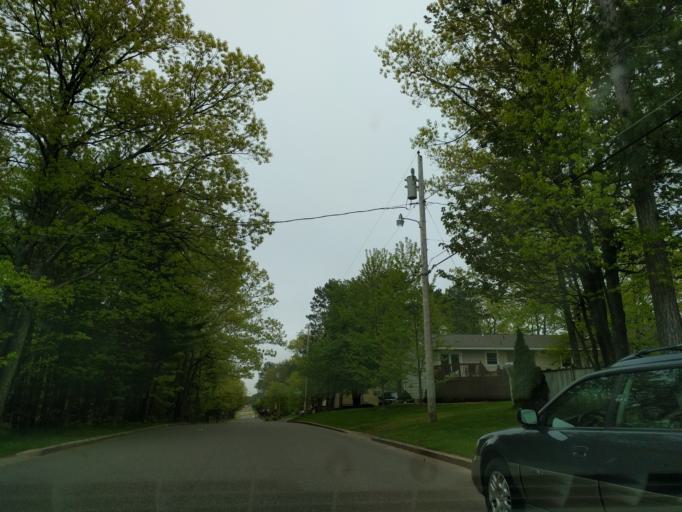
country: US
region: Michigan
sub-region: Marquette County
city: Trowbridge Park
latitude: 46.5604
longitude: -87.4166
